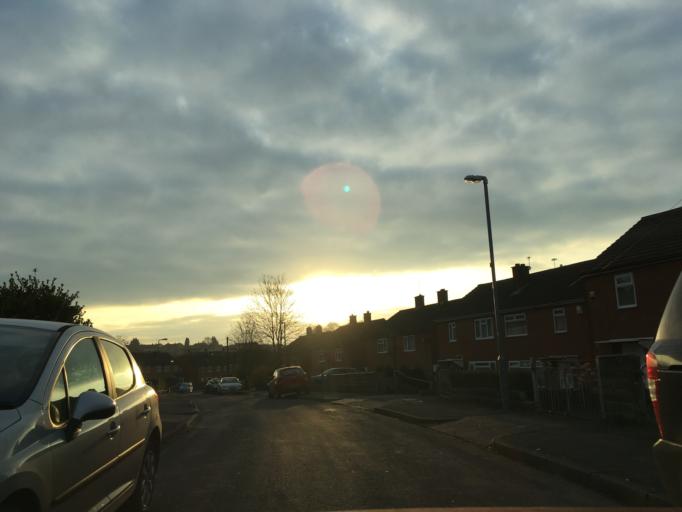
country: GB
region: Wales
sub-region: Newport
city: Marshfield
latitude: 51.5262
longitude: -3.1218
